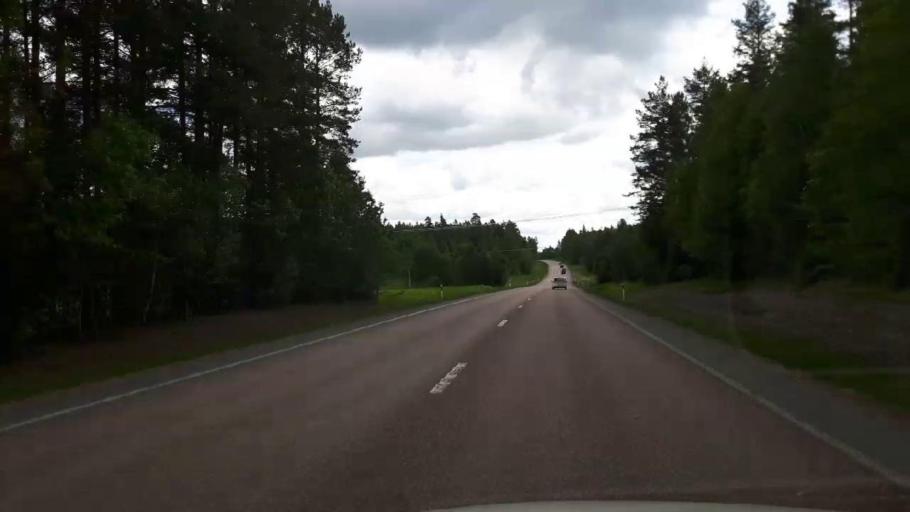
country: SE
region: Dalarna
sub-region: Saters Kommun
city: Saeter
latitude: 60.4884
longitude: 15.7665
